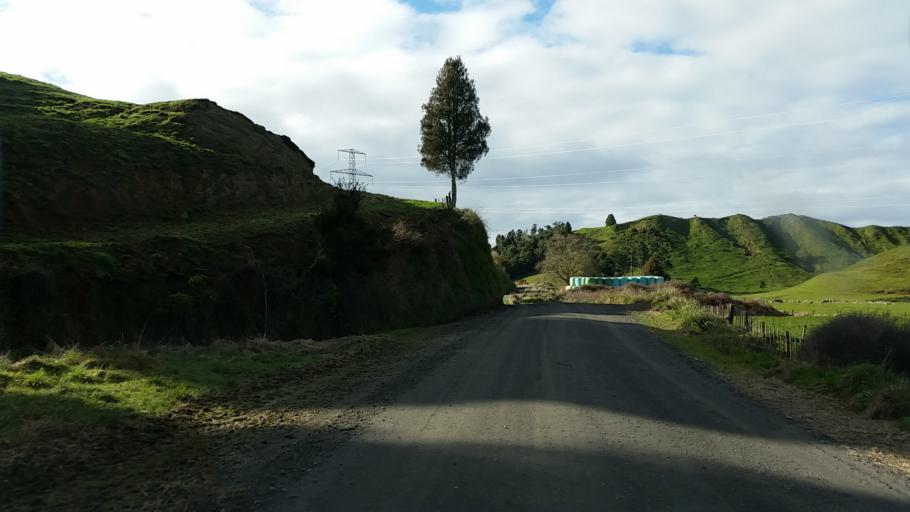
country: NZ
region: Taranaki
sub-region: South Taranaki District
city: Eltham
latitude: -39.2570
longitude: 174.5132
